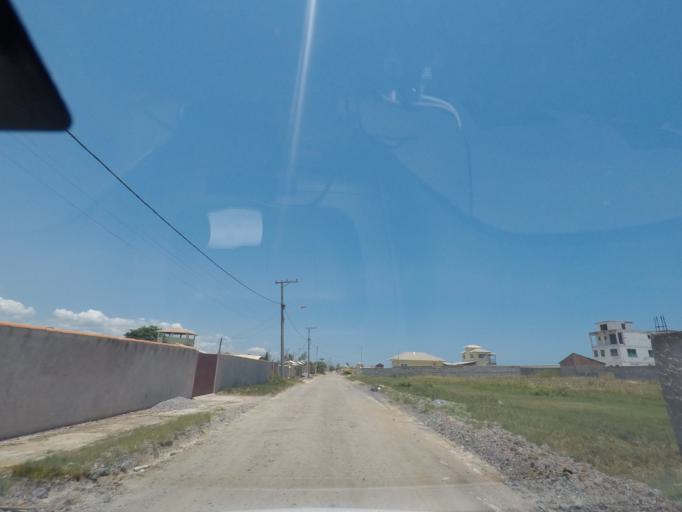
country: BR
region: Rio de Janeiro
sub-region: Niteroi
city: Niteroi
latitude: -22.9683
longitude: -42.9742
